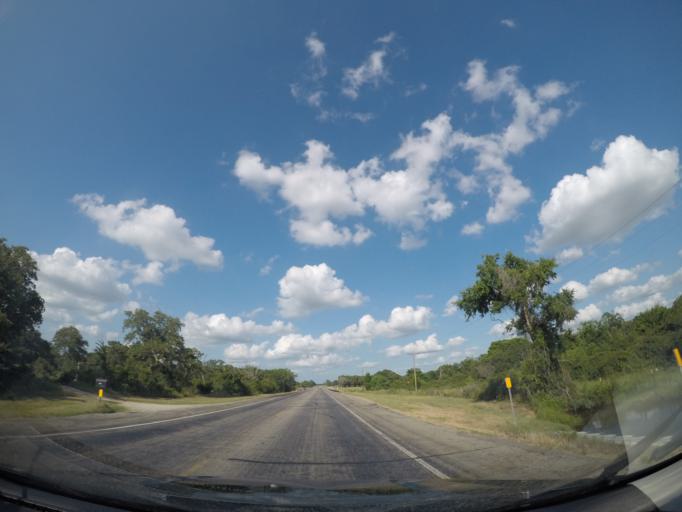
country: US
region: Texas
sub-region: Lavaca County
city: Hallettsville
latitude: 29.4500
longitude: -96.9085
